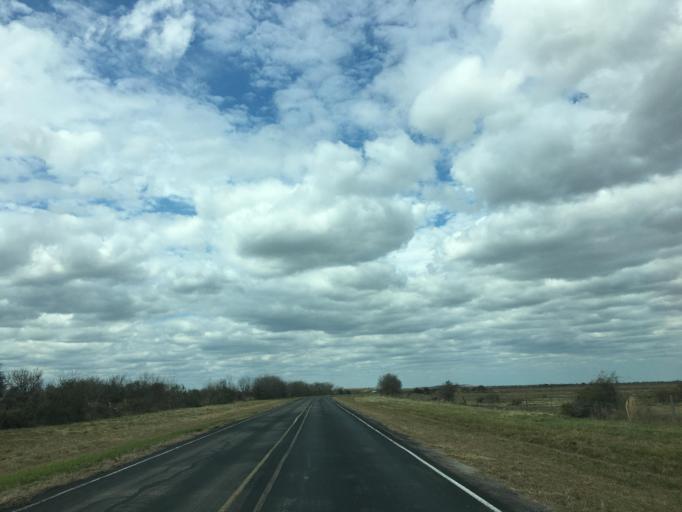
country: US
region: Texas
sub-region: Brazoria County
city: Oyster Creek
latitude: 29.0602
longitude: -95.2795
